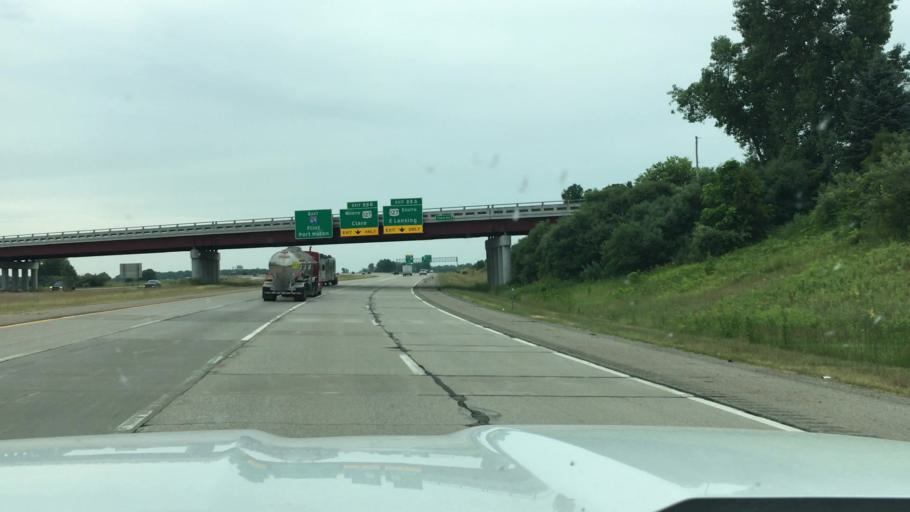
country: US
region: Michigan
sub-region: Clinton County
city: DeWitt
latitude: 42.8139
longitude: -84.5192
